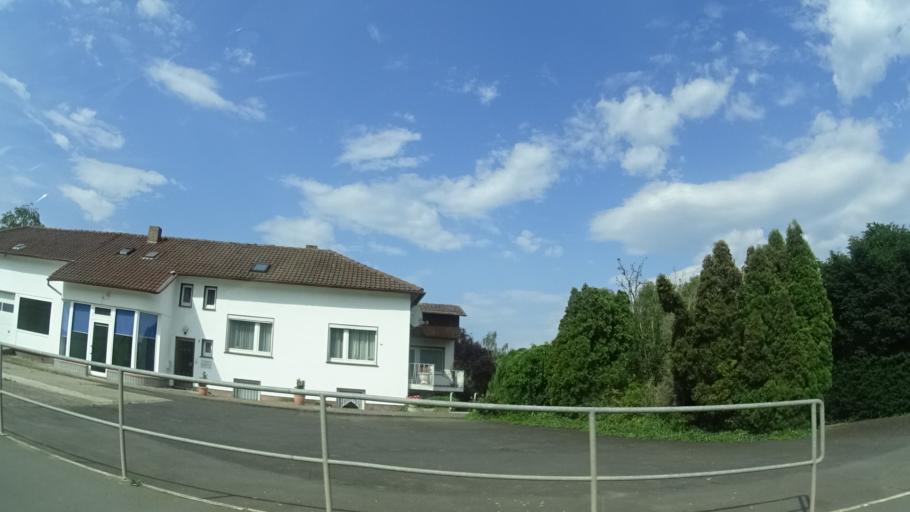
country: DE
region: Hesse
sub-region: Regierungsbezirk Kassel
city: Bad Wildungen
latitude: 51.1597
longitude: 9.1217
